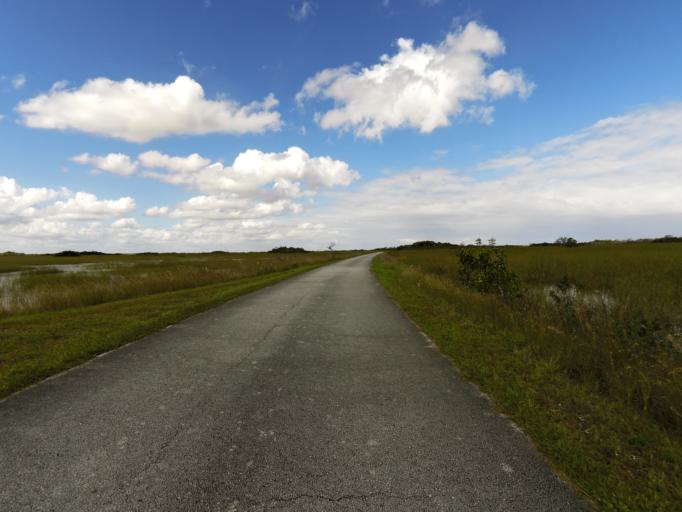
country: US
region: Florida
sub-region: Miami-Dade County
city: The Hammocks
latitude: 25.7297
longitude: -80.7596
